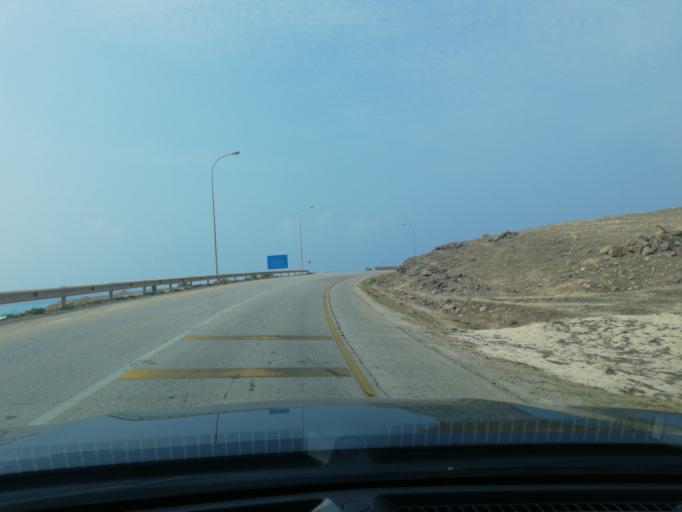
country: OM
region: Zufar
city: Salalah
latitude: 16.8897
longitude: 53.8222
